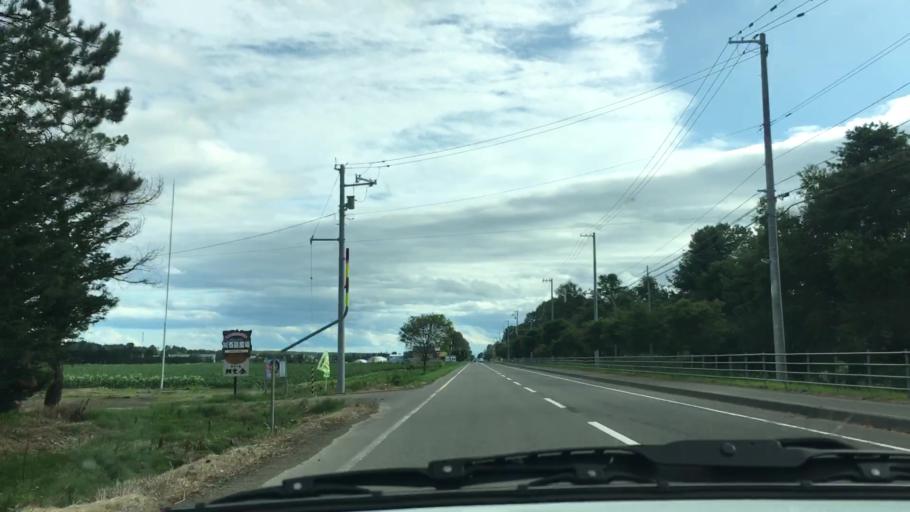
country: JP
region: Hokkaido
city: Otofuke
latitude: 43.2475
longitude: 143.2984
